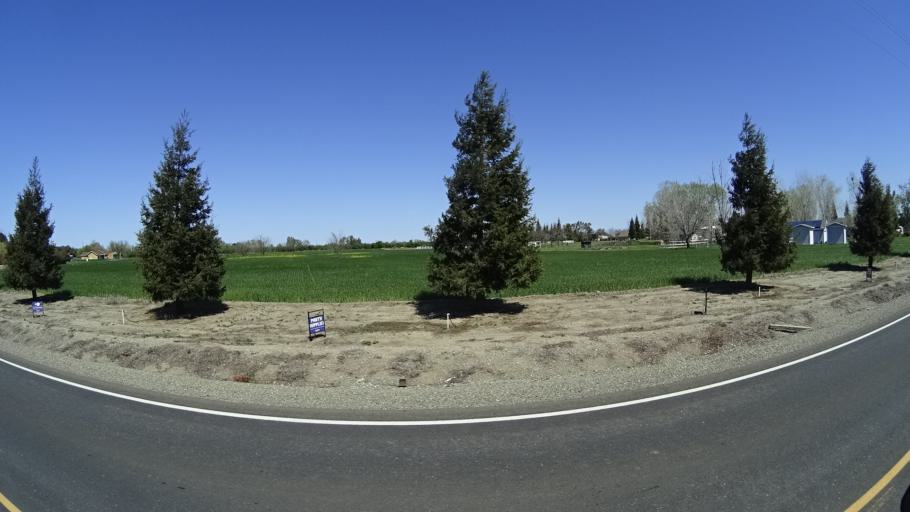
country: US
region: California
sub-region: Glenn County
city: Orland
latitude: 39.7631
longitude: -122.2374
